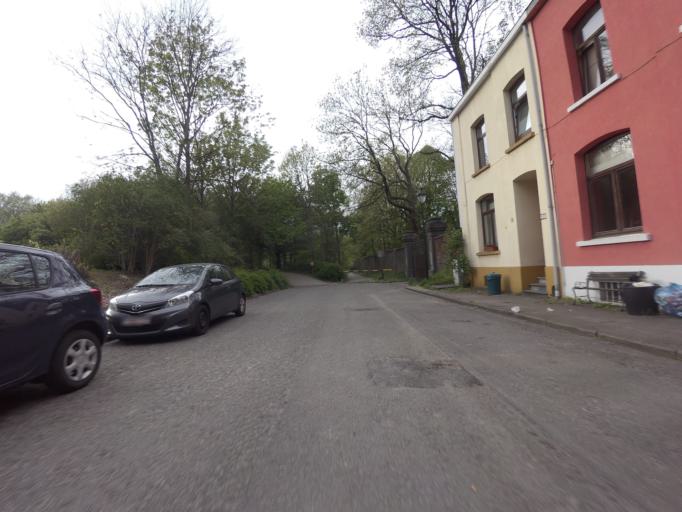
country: BE
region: Flanders
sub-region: Provincie Vlaams-Brabant
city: Diegem
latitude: 50.8681
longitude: 4.4118
